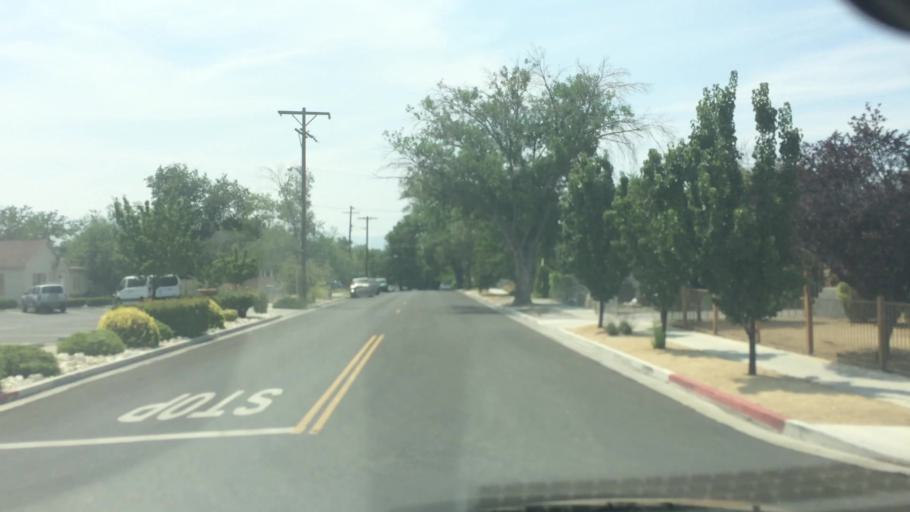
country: US
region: Nevada
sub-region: Washoe County
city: Reno
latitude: 39.5164
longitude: -119.8048
